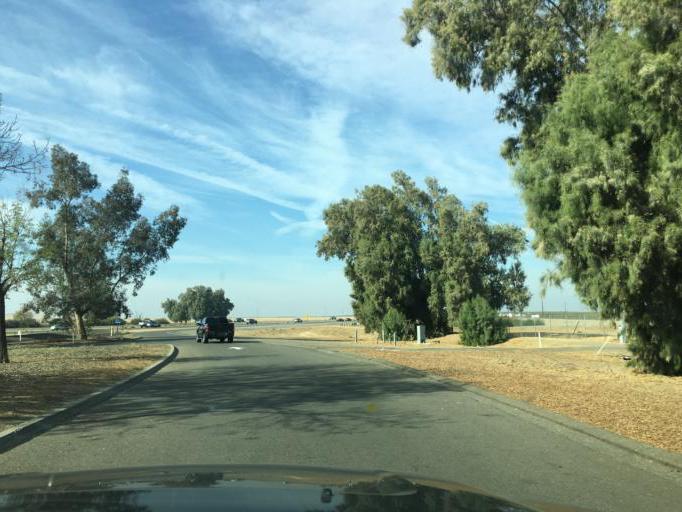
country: US
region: California
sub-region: Kings County
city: Avenal
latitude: 36.0903
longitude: -120.1134
